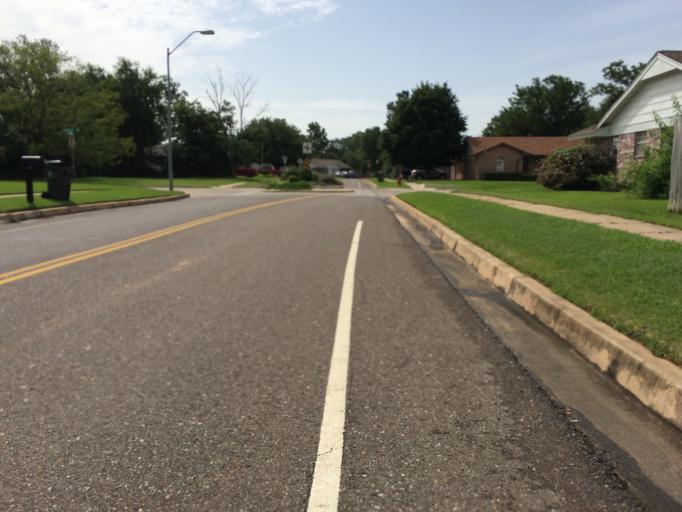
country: US
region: Oklahoma
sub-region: Cleveland County
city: Norman
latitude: 35.2009
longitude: -97.4121
